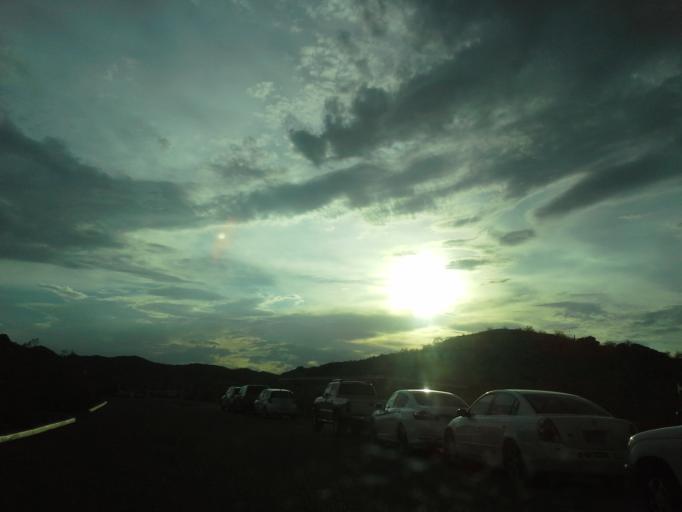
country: US
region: Arizona
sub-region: Maricopa County
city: Guadalupe
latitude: 33.3630
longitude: -111.9849
